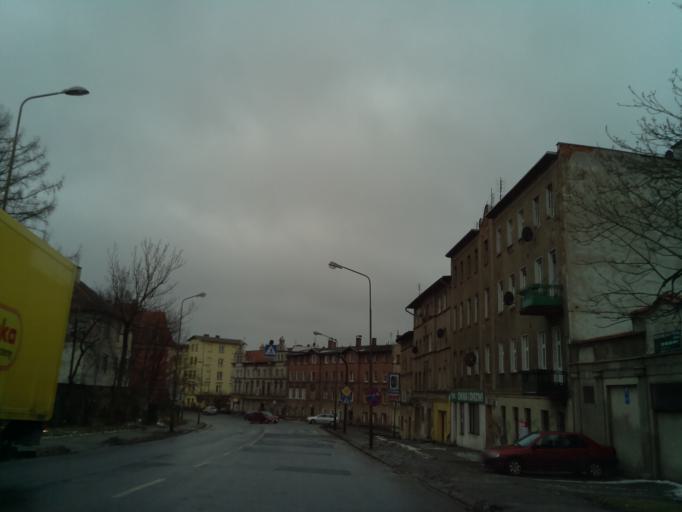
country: PL
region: Lower Silesian Voivodeship
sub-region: Powiat walbrzyski
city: Szczawno-Zdroj
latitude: 50.8202
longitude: 16.3009
